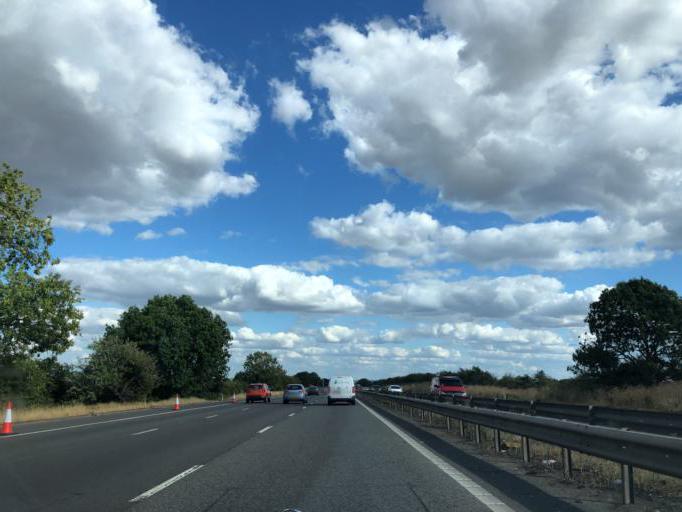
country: GB
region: England
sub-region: Milton Keynes
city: Hanslope
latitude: 52.1289
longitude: -0.8197
